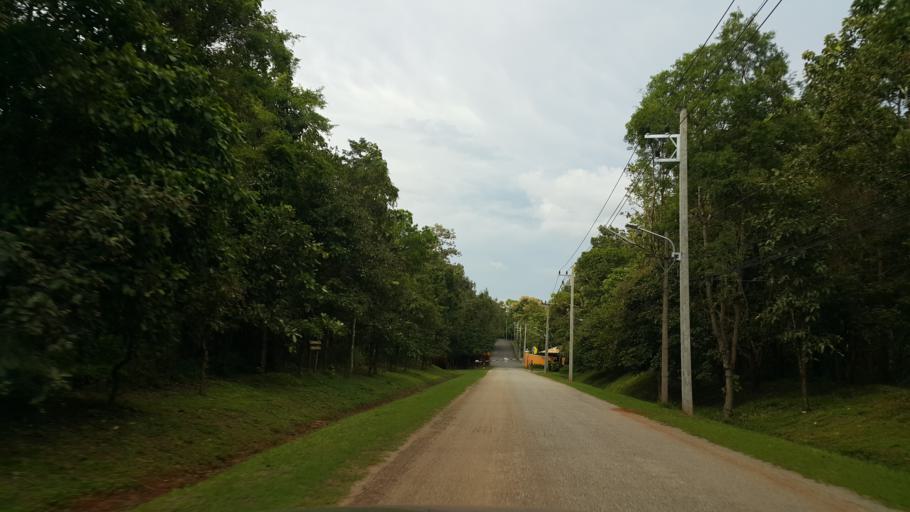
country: TH
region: Chiang Mai
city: Mae On
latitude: 18.8960
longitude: 99.2221
